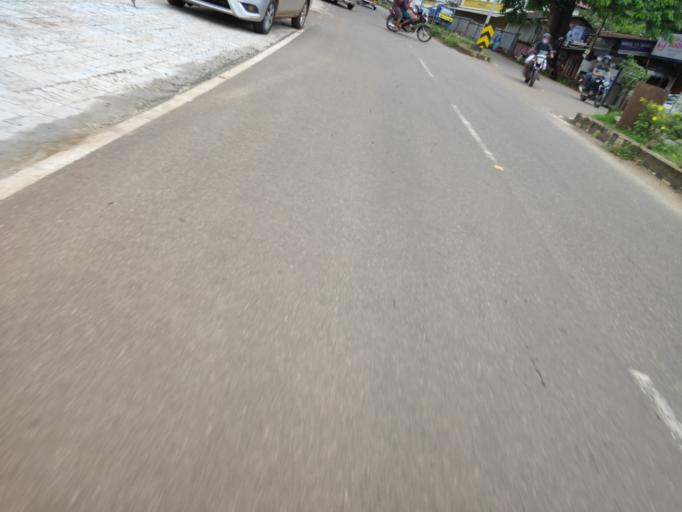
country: IN
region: Kerala
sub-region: Malappuram
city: Manjeri
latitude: 11.1964
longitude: 76.2334
